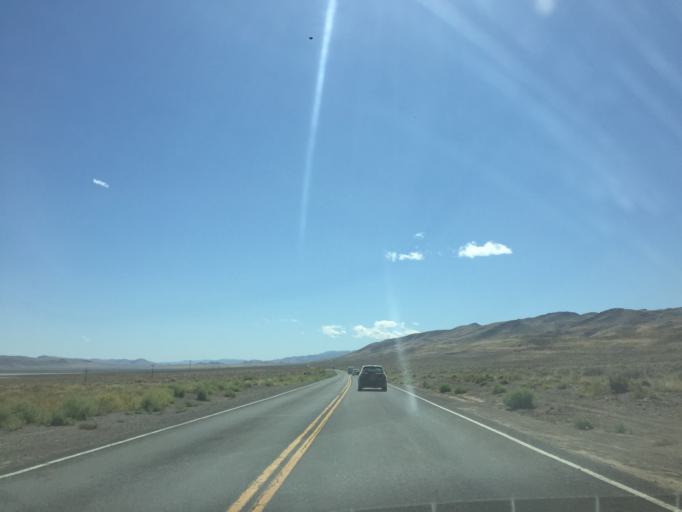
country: US
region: Nevada
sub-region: Lyon County
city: Fernley
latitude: 40.0475
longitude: -119.3841
